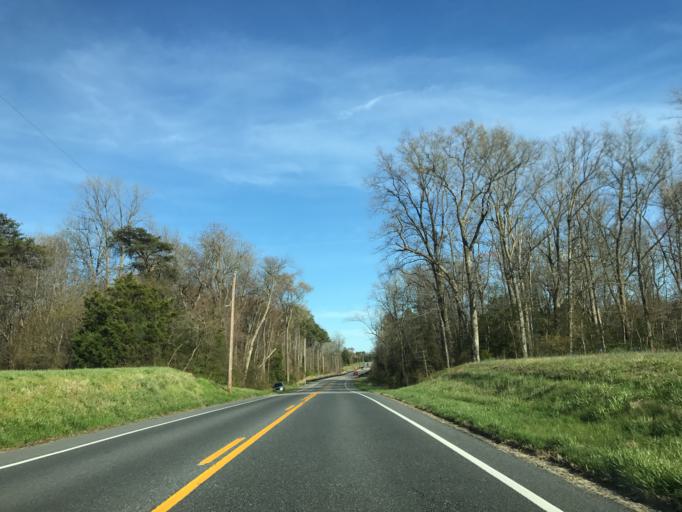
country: US
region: Maryland
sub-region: Caroline County
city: Greensboro
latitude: 39.0317
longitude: -75.7624
